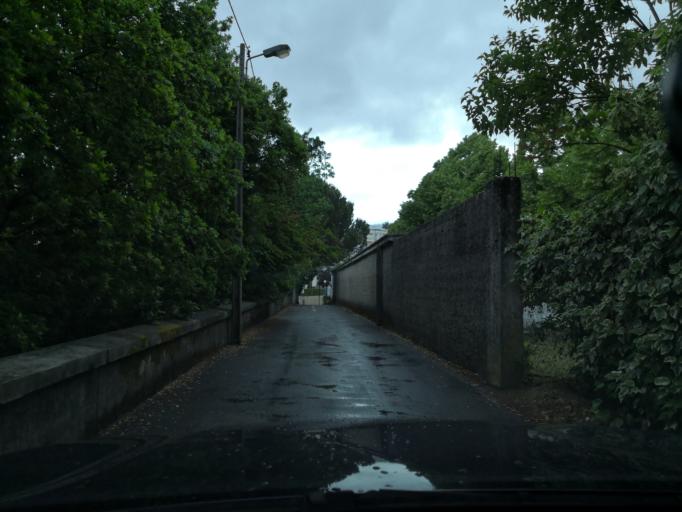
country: PT
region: Vila Real
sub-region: Vila Real
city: Vila Real
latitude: 41.3026
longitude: -7.7368
